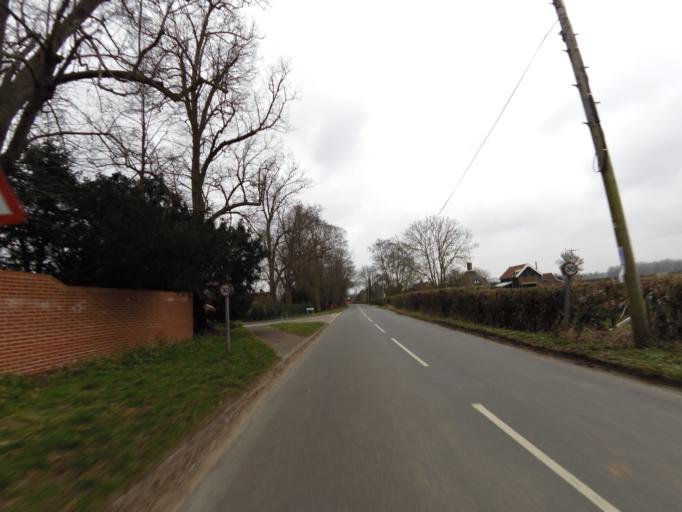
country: GB
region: England
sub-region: Suffolk
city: Framlingham
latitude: 52.1815
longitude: 1.3340
